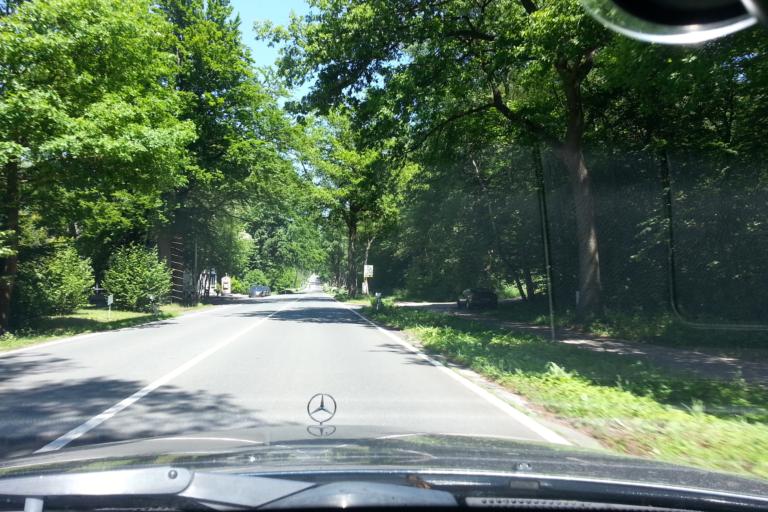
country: DE
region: North Rhine-Westphalia
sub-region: Regierungsbezirk Munster
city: Haltern
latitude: 51.6799
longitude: 7.1822
